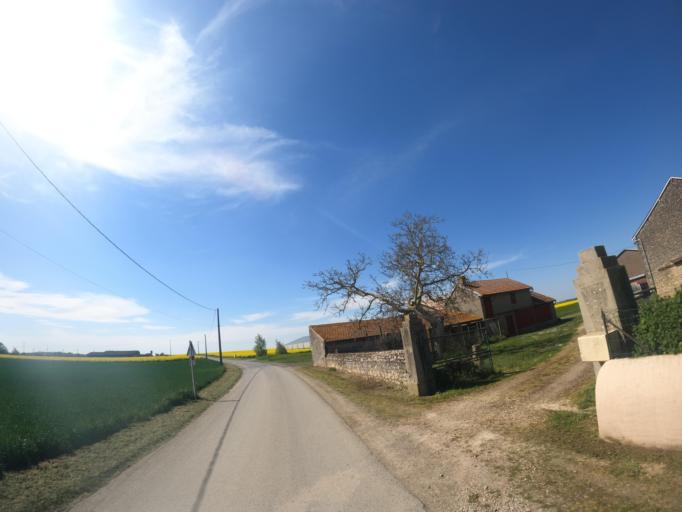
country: FR
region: Poitou-Charentes
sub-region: Departement des Deux-Sevres
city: Airvault
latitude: 46.8796
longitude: -0.1679
